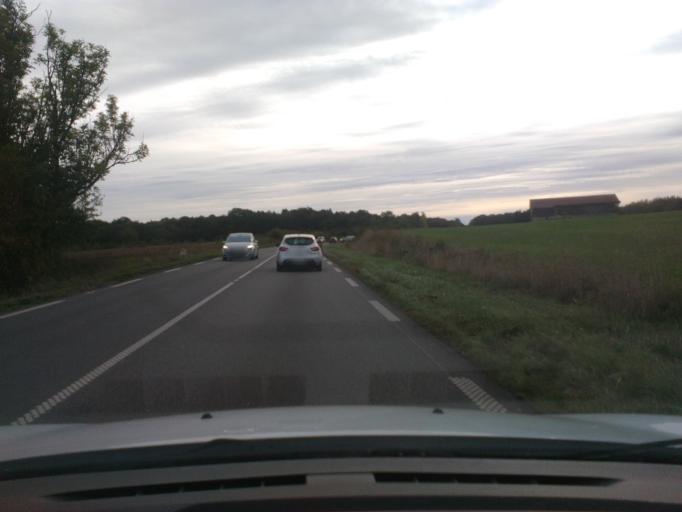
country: FR
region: Lorraine
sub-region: Departement des Vosges
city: Aydoilles
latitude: 48.2707
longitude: 6.5604
